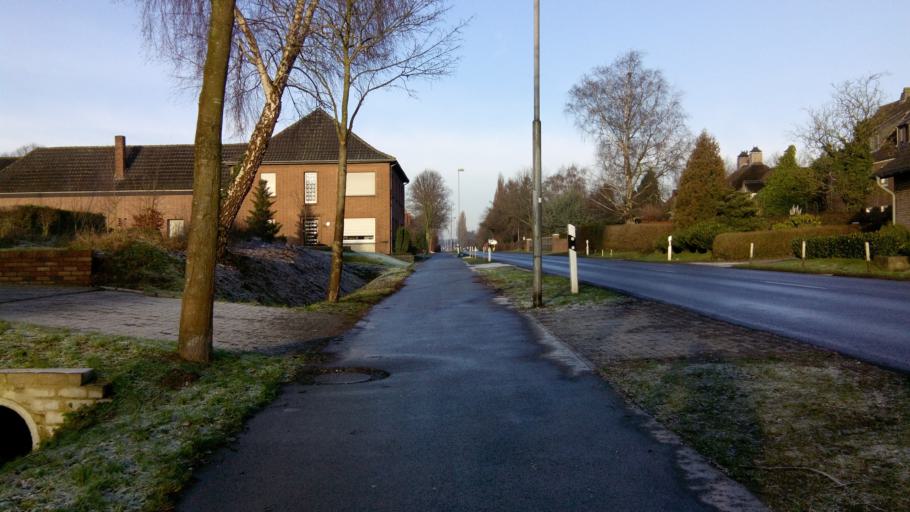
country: NL
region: Gelderland
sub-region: Gemeente Groesbeek
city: De Horst
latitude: 51.8014
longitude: 5.9728
